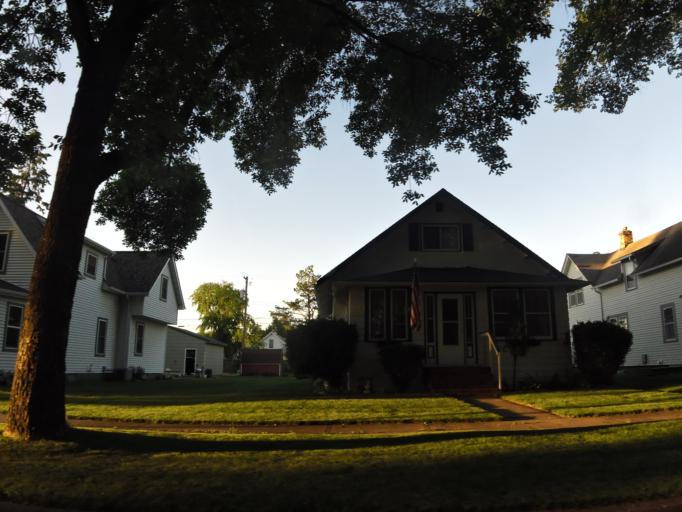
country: US
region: North Dakota
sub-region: Grand Forks County
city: Grand Forks
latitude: 47.9265
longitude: -97.0421
